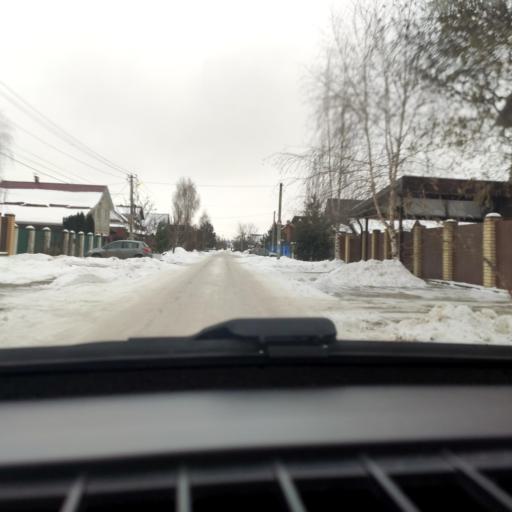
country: RU
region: Voronezj
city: Somovo
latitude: 51.6891
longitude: 39.3093
